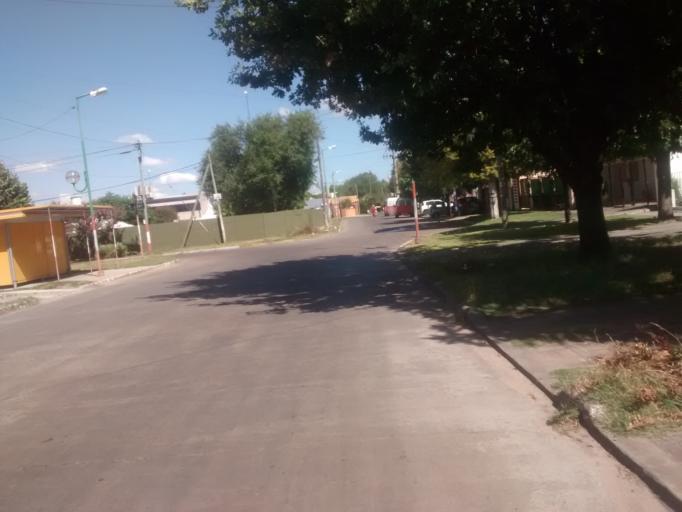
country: AR
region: Buenos Aires
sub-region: Partido de La Plata
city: La Plata
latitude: -34.9291
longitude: -57.9032
